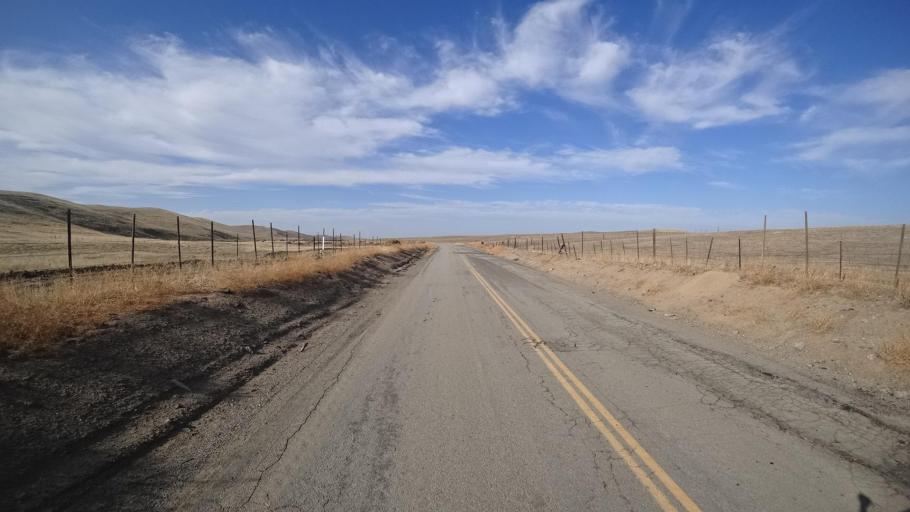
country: US
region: California
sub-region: Tulare County
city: Richgrove
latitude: 35.6267
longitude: -118.9927
